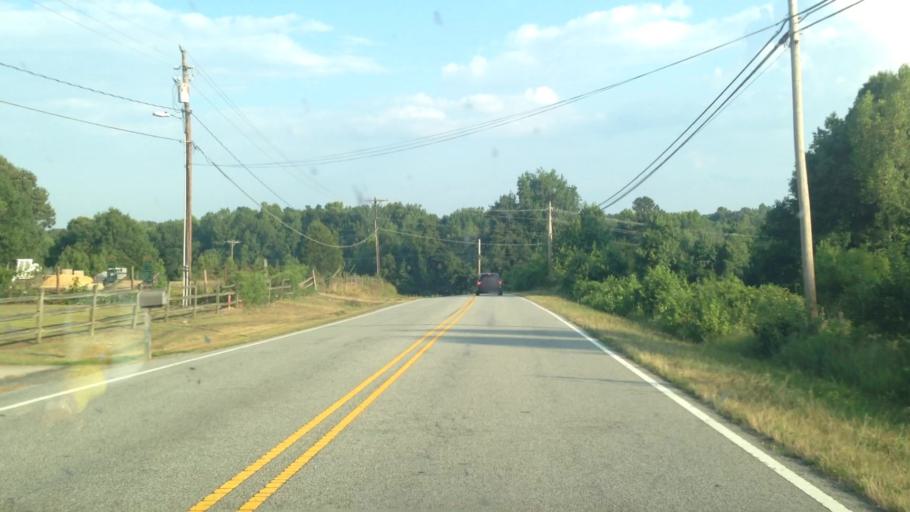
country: US
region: North Carolina
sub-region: Guilford County
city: High Point
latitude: 35.9524
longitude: -80.0709
